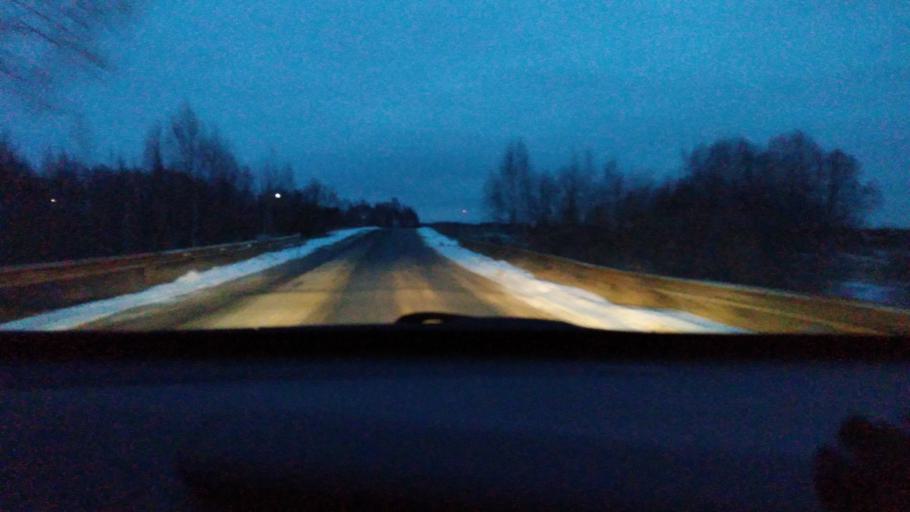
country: RU
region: Moskovskaya
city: Meshcherino
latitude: 55.3131
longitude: 38.3297
